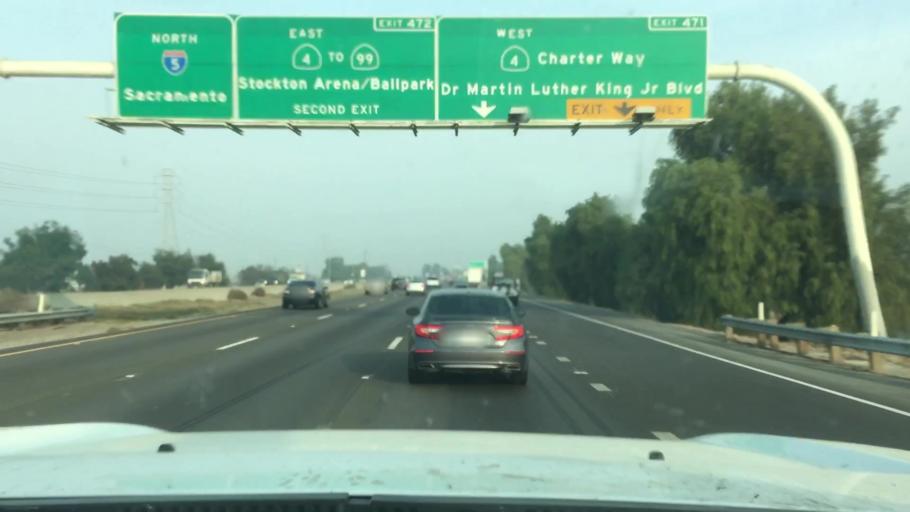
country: US
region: California
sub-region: San Joaquin County
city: Taft Mosswood
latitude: 37.9305
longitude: -121.2957
